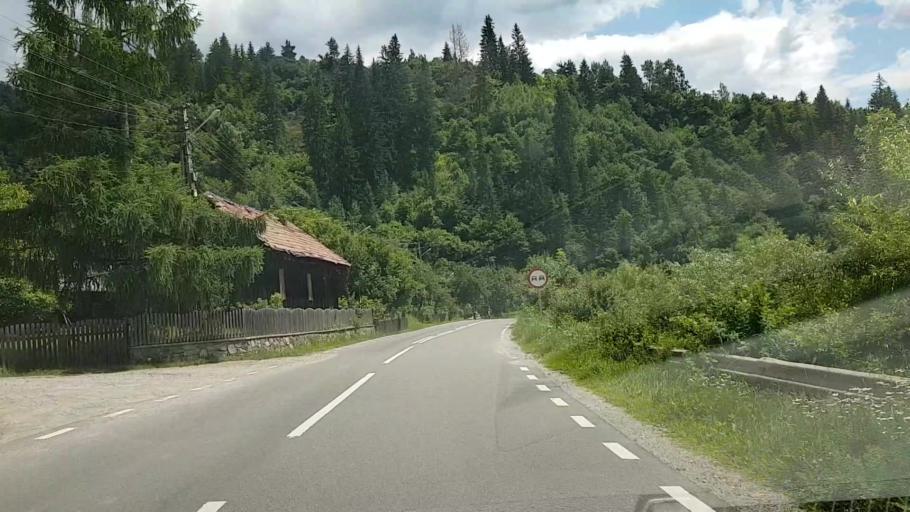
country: RO
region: Suceava
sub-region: Comuna Brosteni
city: Brosteni
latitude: 47.2543
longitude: 25.6945
